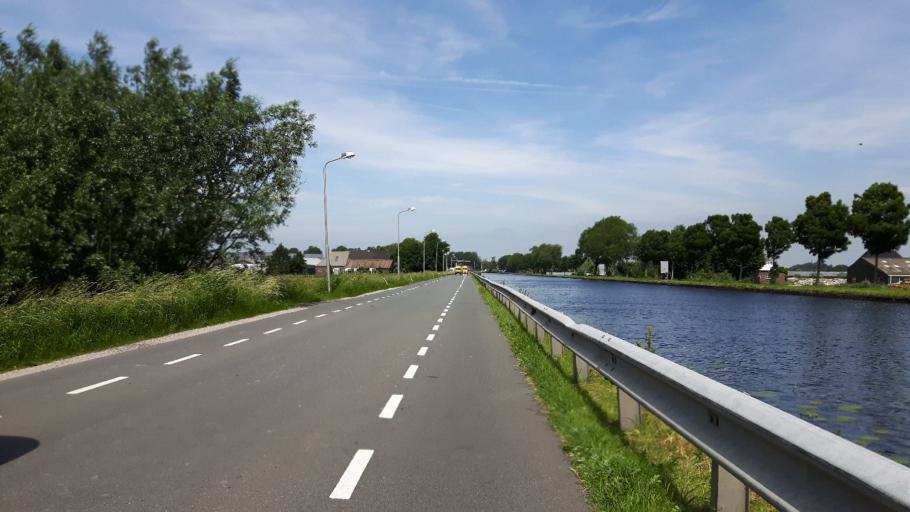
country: NL
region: South Holland
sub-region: Gemeente Nieuwkoop
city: Nieuwkoop
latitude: 52.1893
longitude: 4.7343
